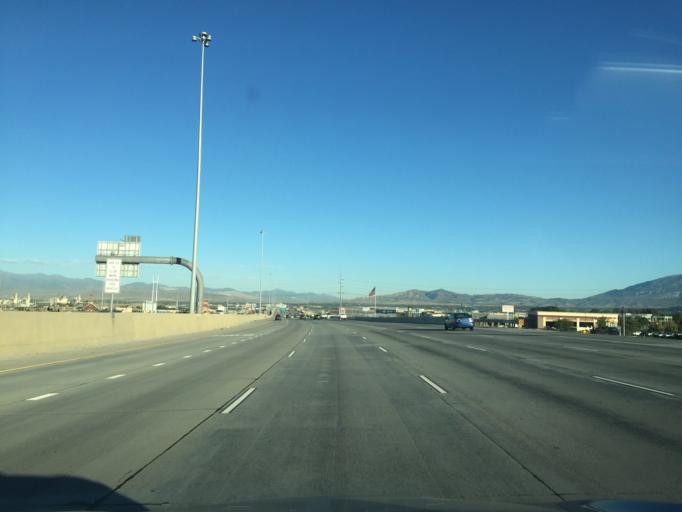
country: US
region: Utah
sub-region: Utah County
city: Lindon
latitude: 40.3248
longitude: -111.7296
